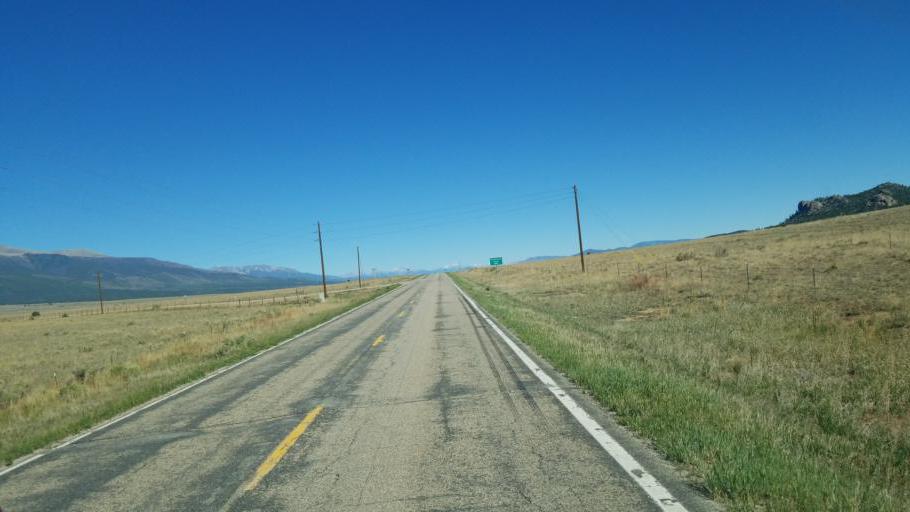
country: US
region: Colorado
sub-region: Custer County
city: Westcliffe
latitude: 38.1977
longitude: -105.5300
